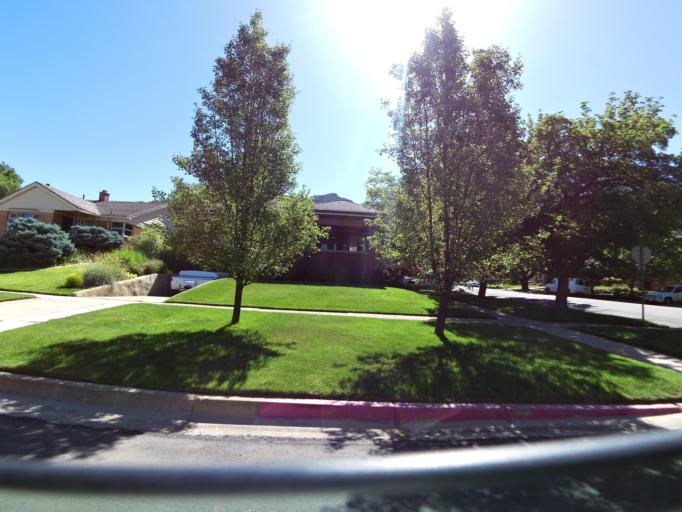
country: US
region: Utah
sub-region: Weber County
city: Ogden
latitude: 41.2183
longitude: -111.9428
